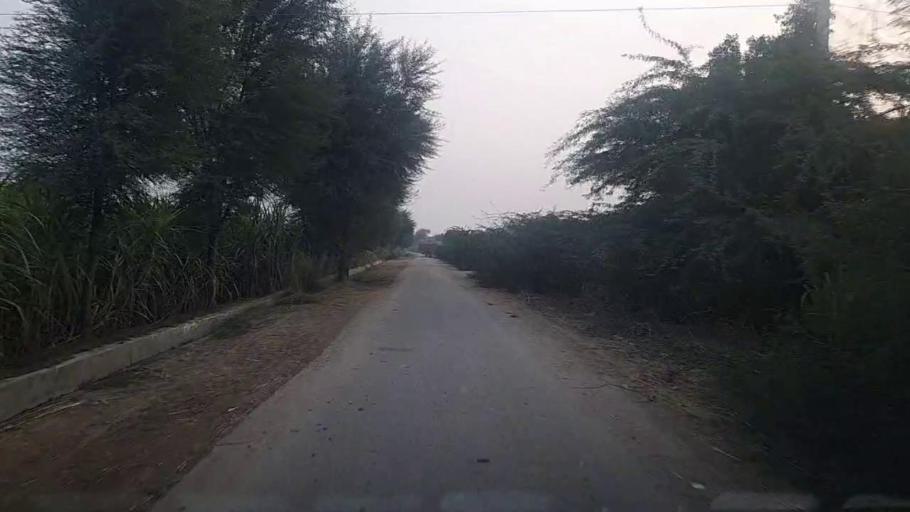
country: PK
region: Sindh
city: Kot Diji
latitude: 27.3435
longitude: 68.6425
